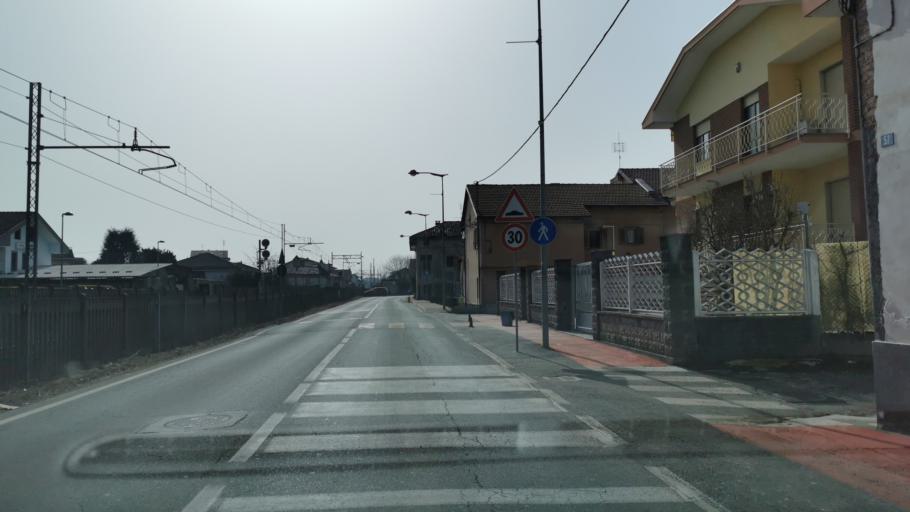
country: IT
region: Piedmont
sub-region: Provincia di Torino
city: Volpiano
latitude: 45.2060
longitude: 7.7803
